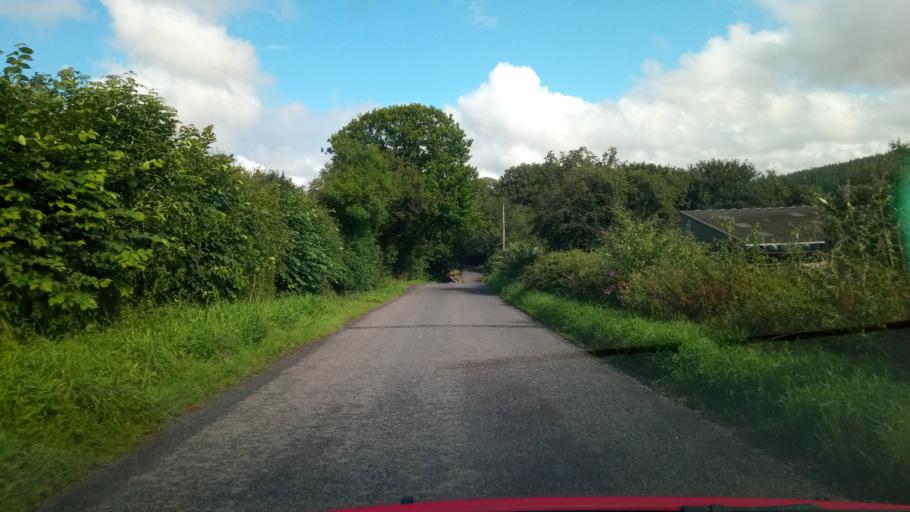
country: GB
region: Scotland
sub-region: The Scottish Borders
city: Earlston
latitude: 55.6460
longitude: -2.6998
